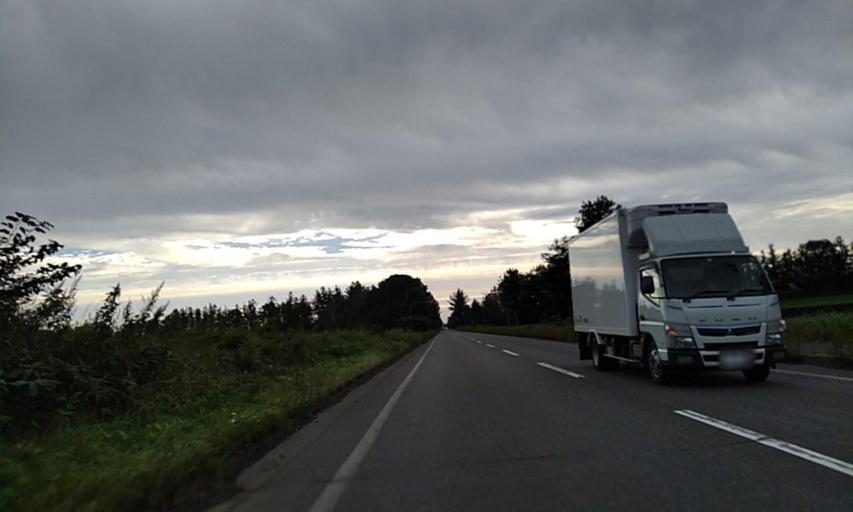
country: JP
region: Hokkaido
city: Otofuke
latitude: 42.9572
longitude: 142.9143
